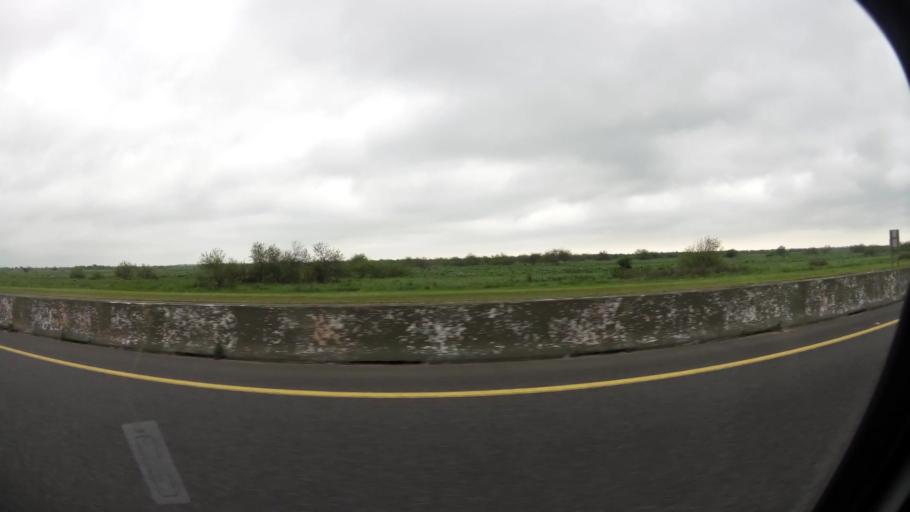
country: AR
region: Buenos Aires
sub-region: Partido de La Plata
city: La Plata
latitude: -34.8655
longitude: -58.0085
